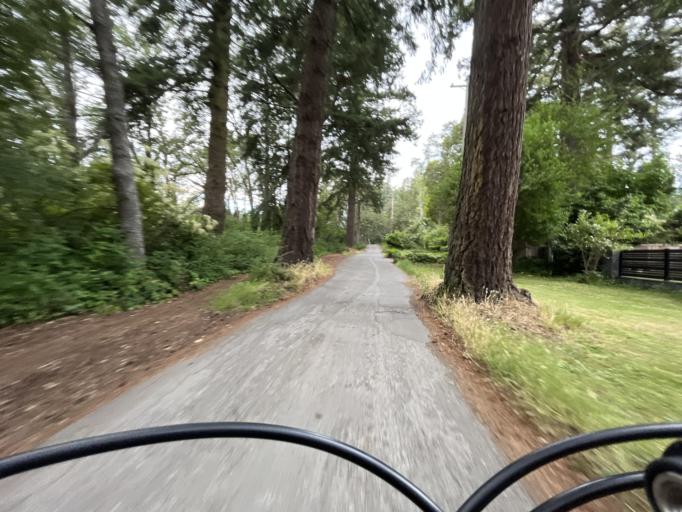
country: CA
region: British Columbia
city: Oak Bay
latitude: 48.4811
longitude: -123.3459
